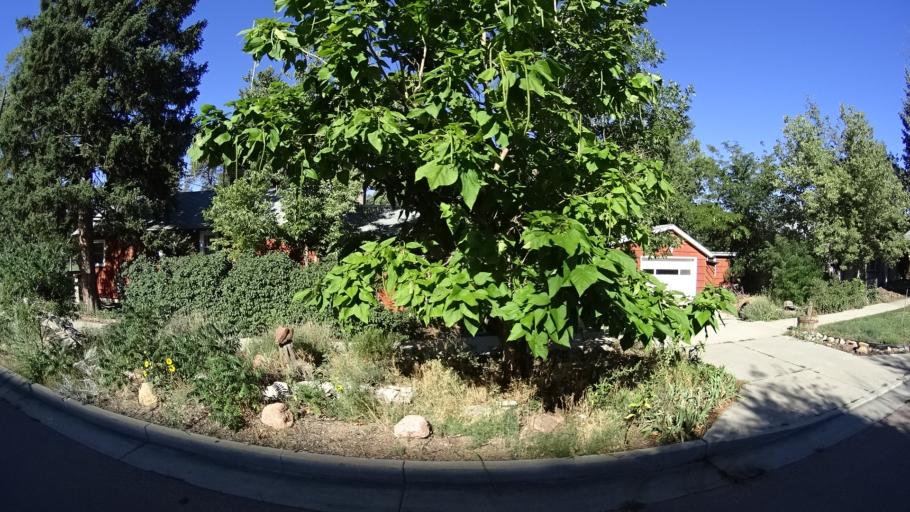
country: US
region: Colorado
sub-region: El Paso County
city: Colorado Springs
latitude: 38.8406
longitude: -104.8004
